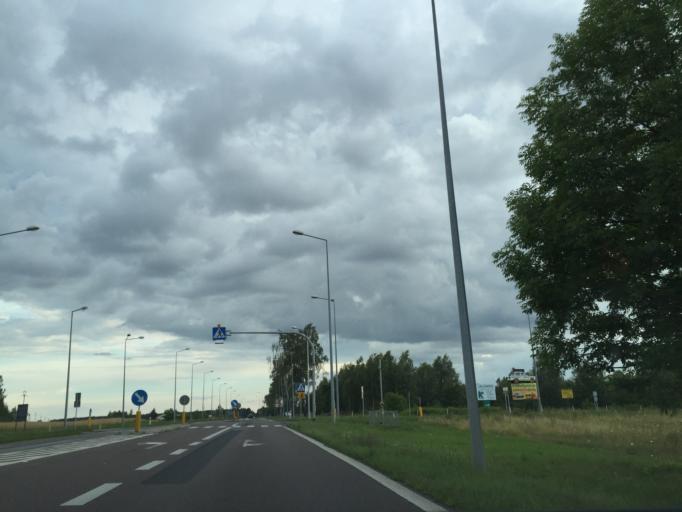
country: PL
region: Lublin Voivodeship
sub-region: Powiat radzynski
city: Borki
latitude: 51.7180
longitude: 22.5279
